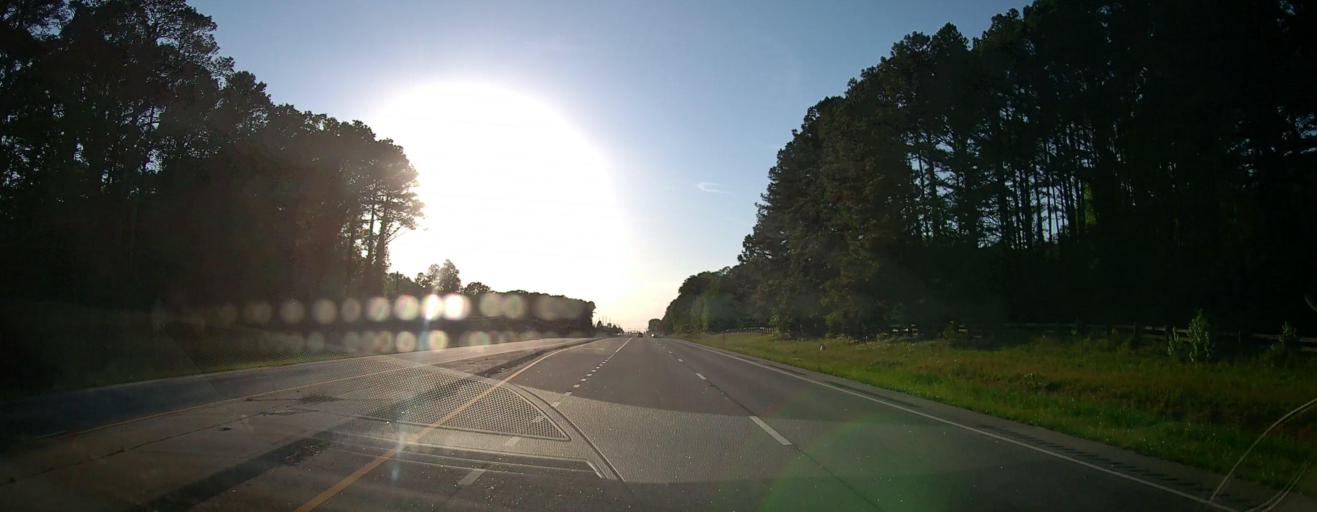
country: US
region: Georgia
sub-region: Newton County
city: Covington
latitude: 33.5950
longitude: -83.8197
